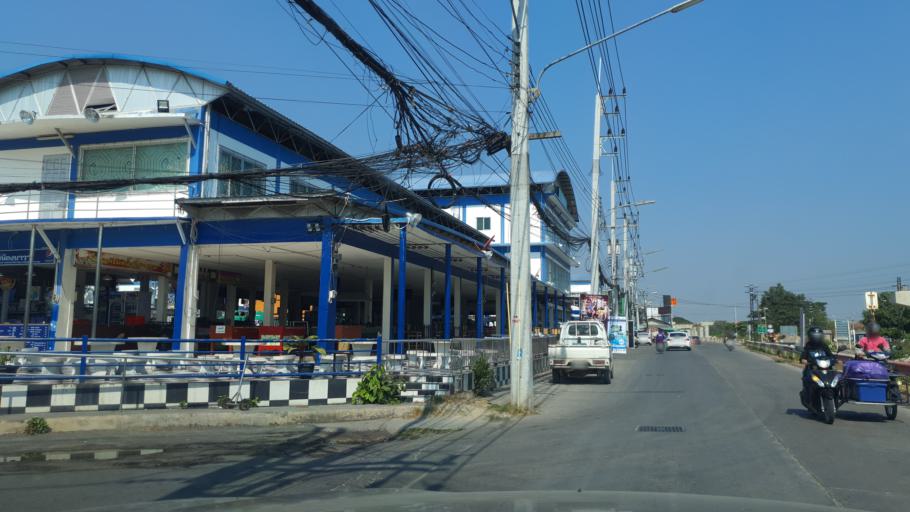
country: TH
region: Prachuap Khiri Khan
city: Hua Hin
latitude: 12.5600
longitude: 99.9562
